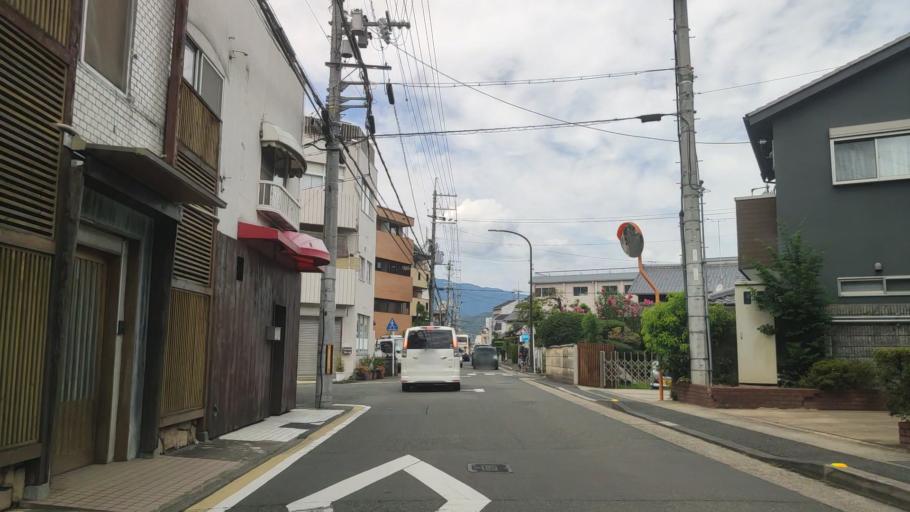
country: JP
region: Kyoto
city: Muko
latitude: 35.0037
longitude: 135.6851
